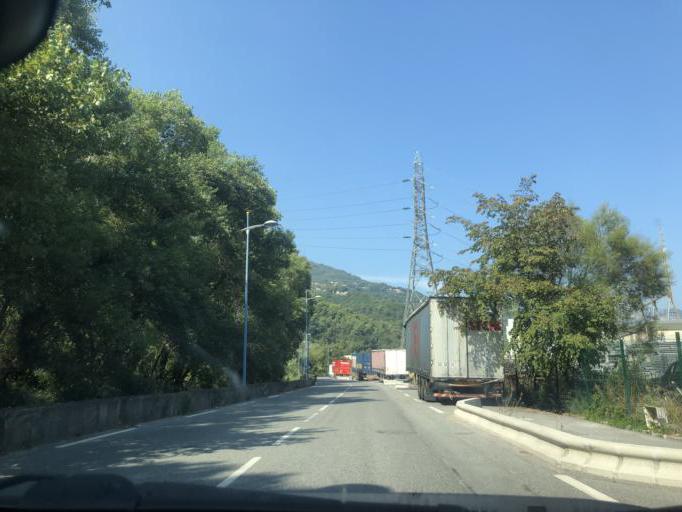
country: FR
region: Provence-Alpes-Cote d'Azur
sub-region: Departement des Alpes-Maritimes
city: Carros
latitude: 43.8017
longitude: 7.1920
